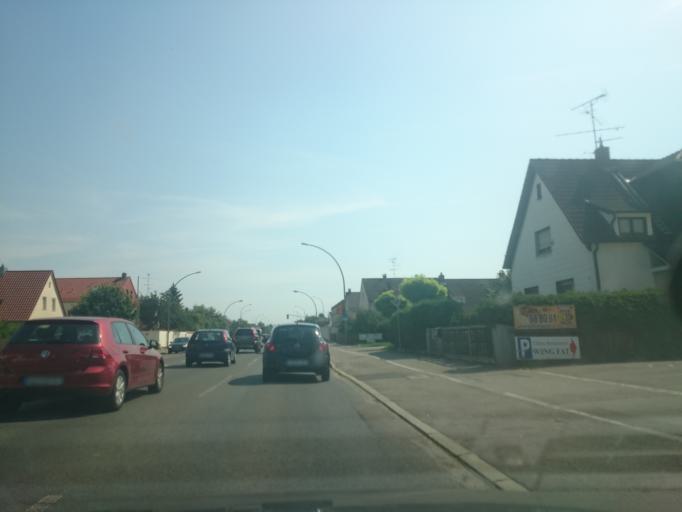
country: DE
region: Bavaria
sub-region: Swabia
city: Konigsbrunn
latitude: 48.2941
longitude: 10.8986
